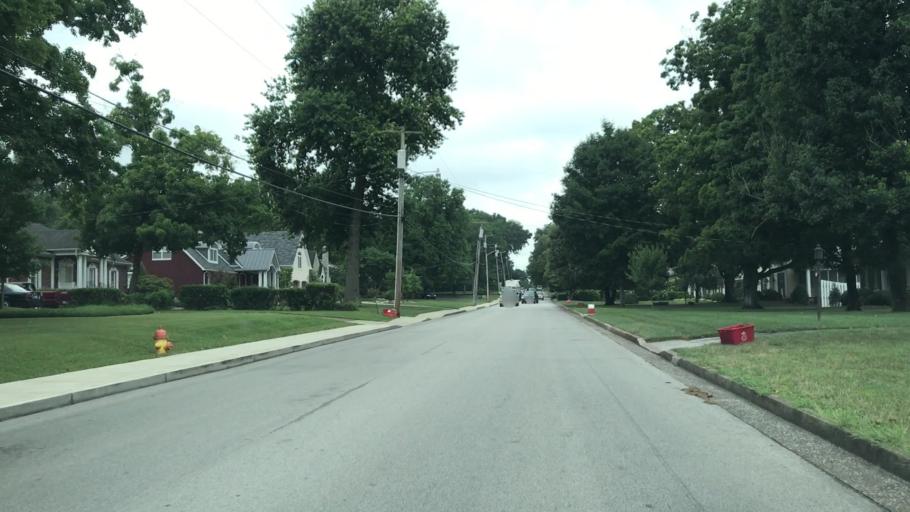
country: US
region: Kentucky
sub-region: Warren County
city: Bowling Green
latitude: 36.9818
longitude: -86.4295
